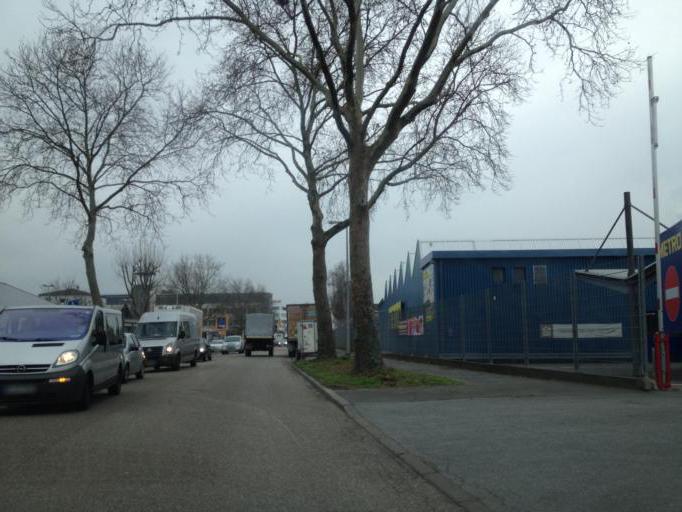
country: DE
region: Rheinland-Pfalz
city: Altrip
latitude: 49.4588
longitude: 8.5018
